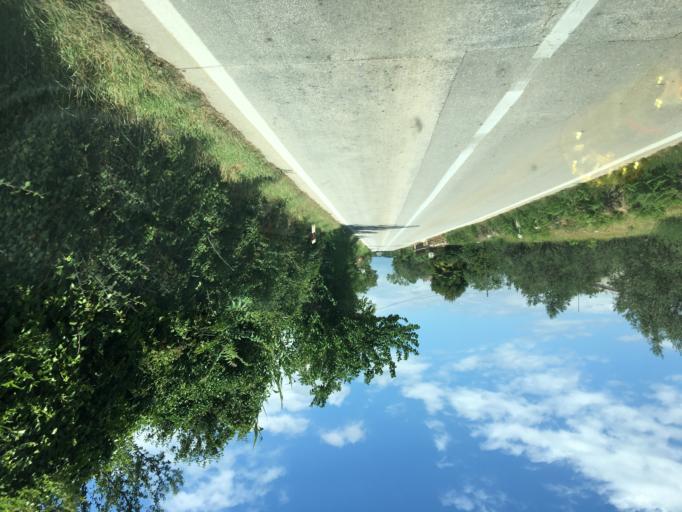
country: HR
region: Istarska
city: Vrsar
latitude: 45.1753
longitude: 13.7418
